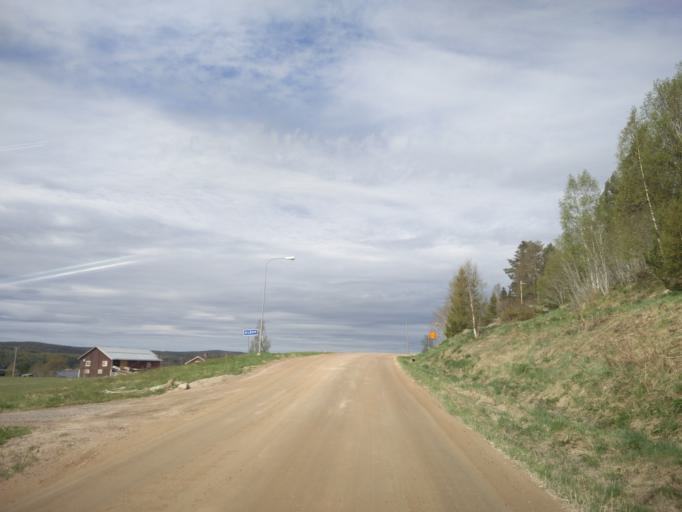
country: SE
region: Vaesternorrland
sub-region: Sundsvalls Kommun
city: Vi
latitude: 62.2765
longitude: 17.1355
